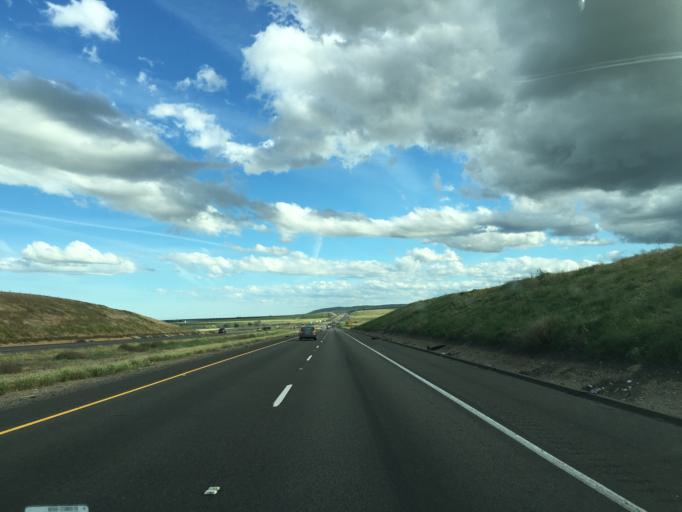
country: US
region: California
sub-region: Merced County
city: Los Banos
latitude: 37.0089
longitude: -120.9239
